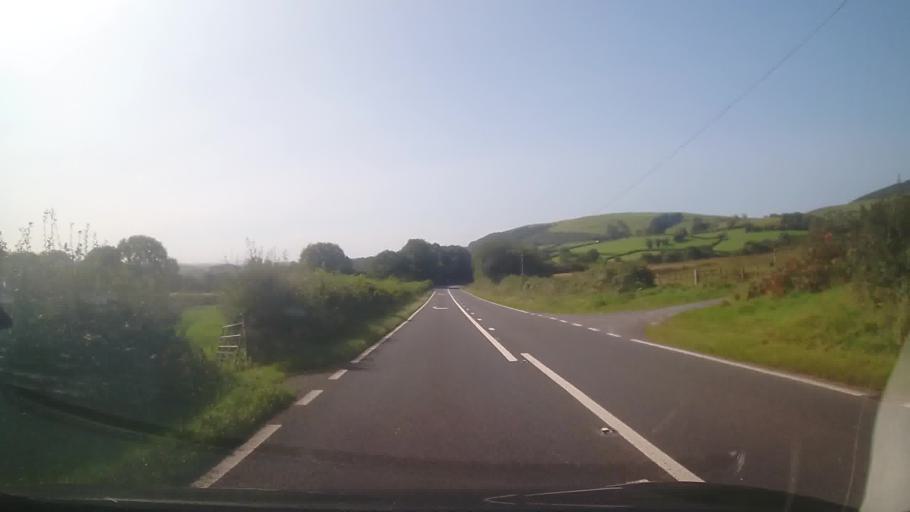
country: GB
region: Wales
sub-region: Sir Powys
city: Rhayader
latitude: 52.1355
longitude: -3.6065
